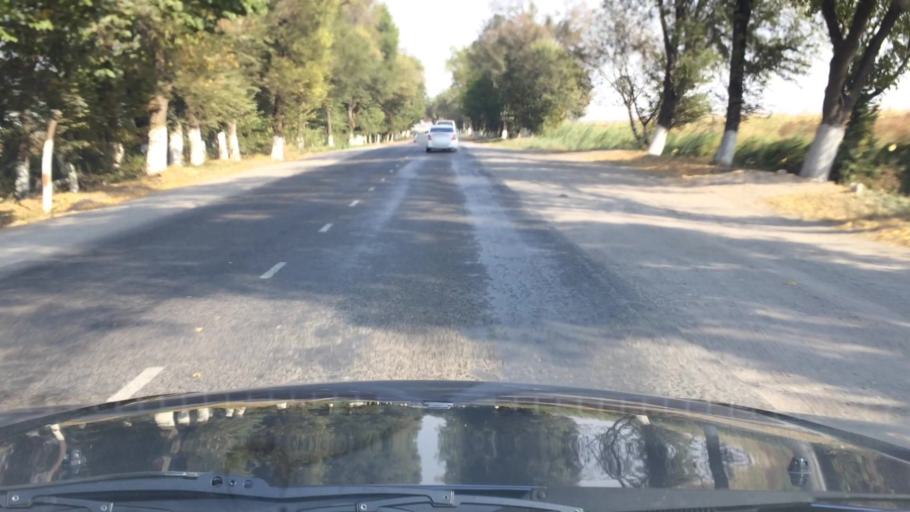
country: KG
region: Chuy
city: Lebedinovka
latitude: 42.8965
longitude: 74.6831
